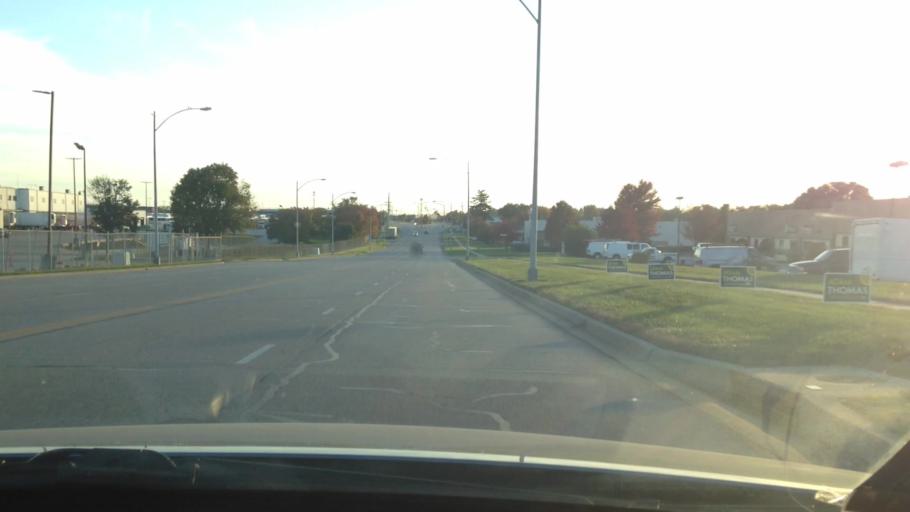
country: US
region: Kansas
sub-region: Johnson County
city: Olathe
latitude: 38.9037
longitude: -94.7850
